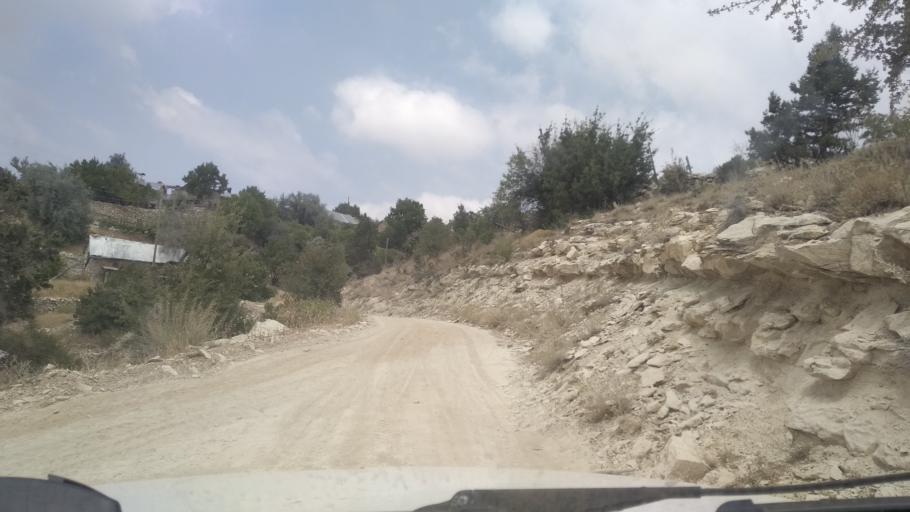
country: TR
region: Mersin
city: Sarikavak
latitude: 36.6007
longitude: 33.7258
